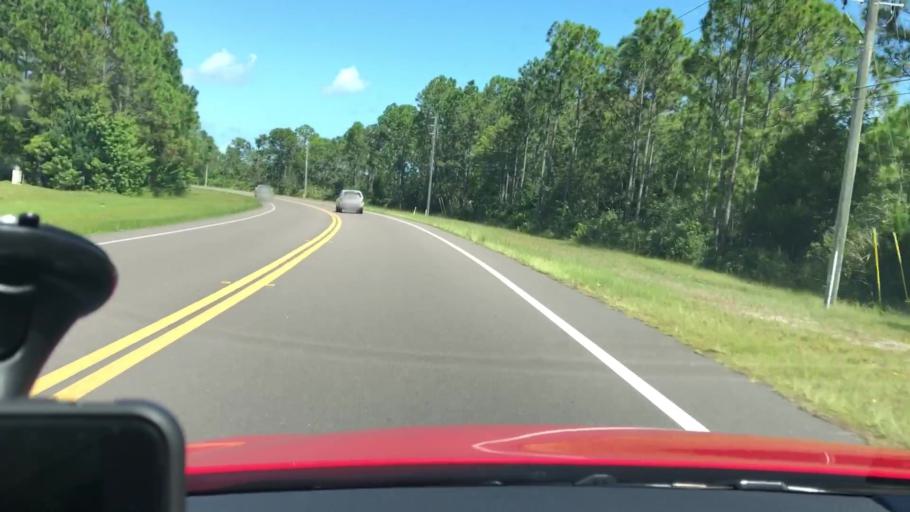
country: US
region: Florida
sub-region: Volusia County
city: Ormond Beach
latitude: 29.2540
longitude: -81.0998
